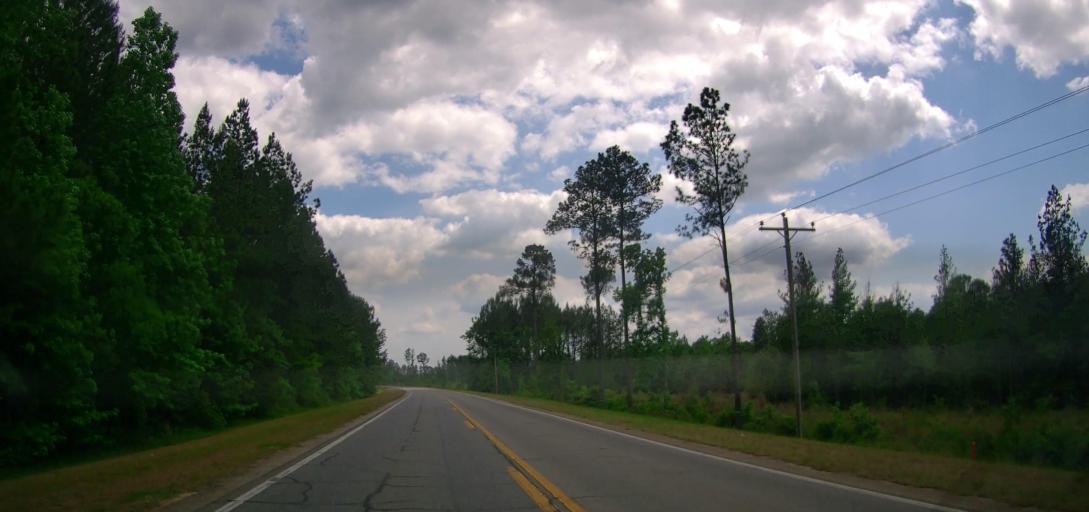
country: US
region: Georgia
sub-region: Laurens County
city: East Dublin
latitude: 32.4930
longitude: -82.8283
